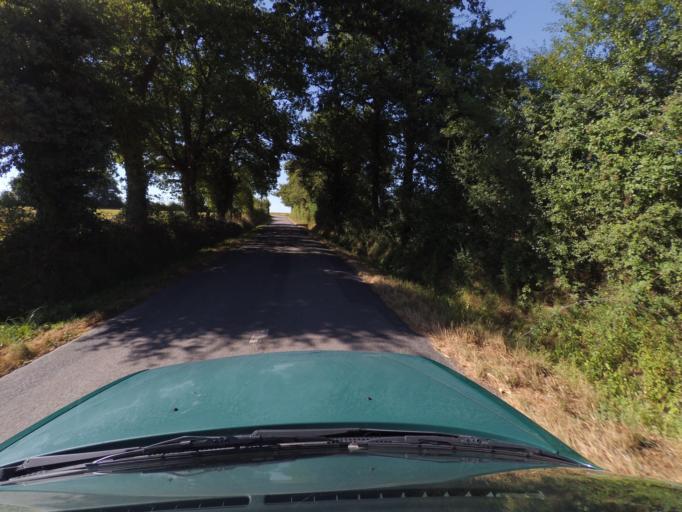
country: FR
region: Pays de la Loire
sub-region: Departement de la Loire-Atlantique
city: Aigrefeuille-sur-Maine
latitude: 47.0955
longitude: -1.4192
